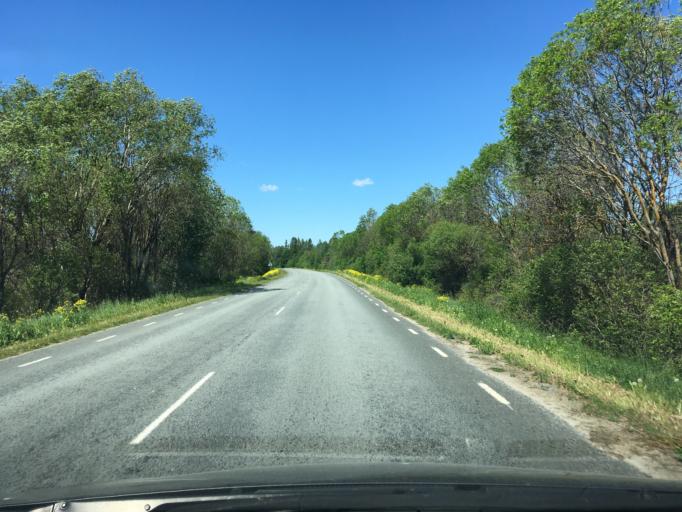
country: EE
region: Harju
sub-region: Rae vald
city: Vaida
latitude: 59.1896
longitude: 25.0046
